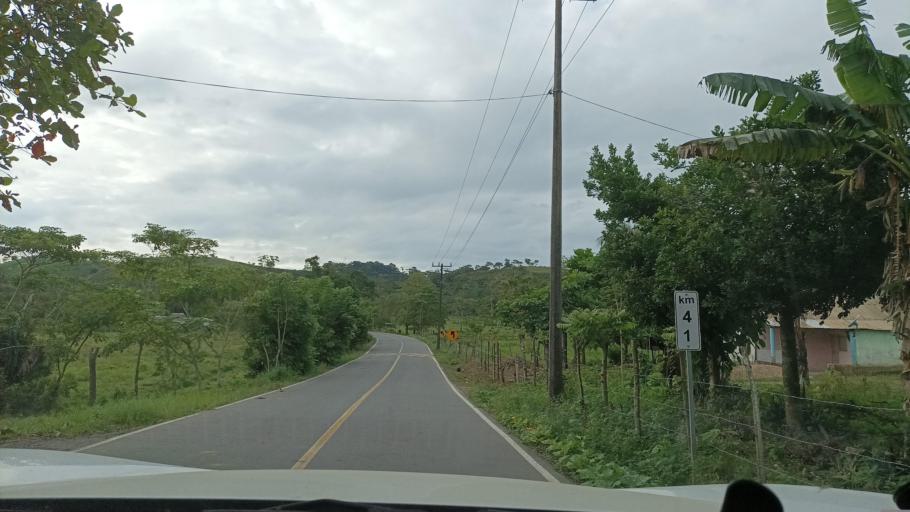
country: MX
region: Veracruz
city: Hidalgotitlan
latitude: 17.7213
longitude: -94.4817
